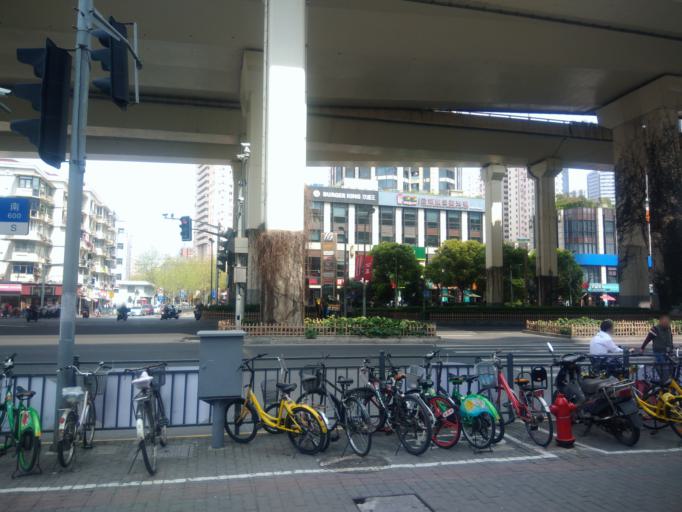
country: CN
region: Shanghai Shi
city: Luwan
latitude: 31.2010
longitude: 121.4718
